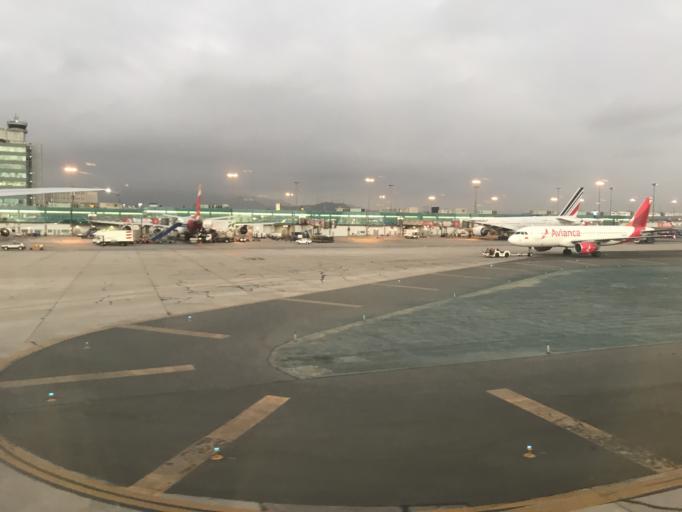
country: PE
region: Callao
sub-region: Callao
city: Callao
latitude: -12.0252
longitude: -77.1106
